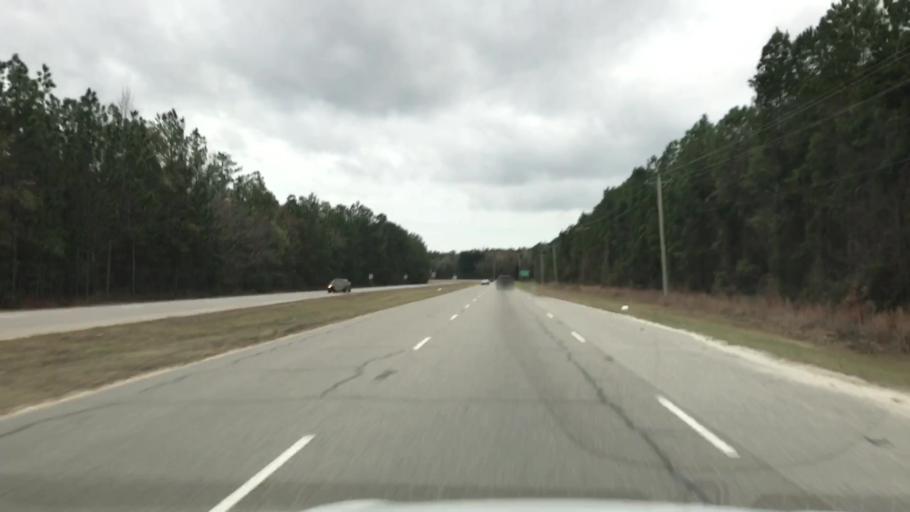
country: US
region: South Carolina
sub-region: Georgetown County
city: Georgetown
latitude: 33.2983
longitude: -79.3433
